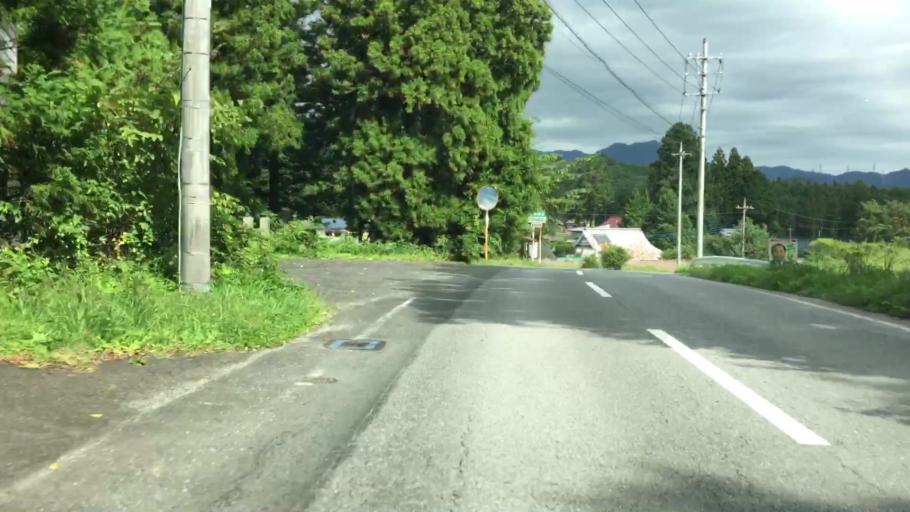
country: JP
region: Tochigi
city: Nikko
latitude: 36.7584
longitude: 139.6618
